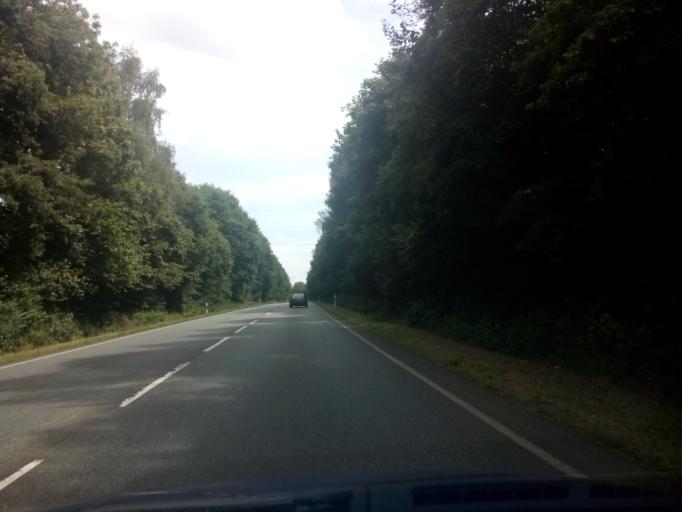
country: DE
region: Lower Saxony
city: Ritterhude
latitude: 53.1808
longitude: 8.7178
